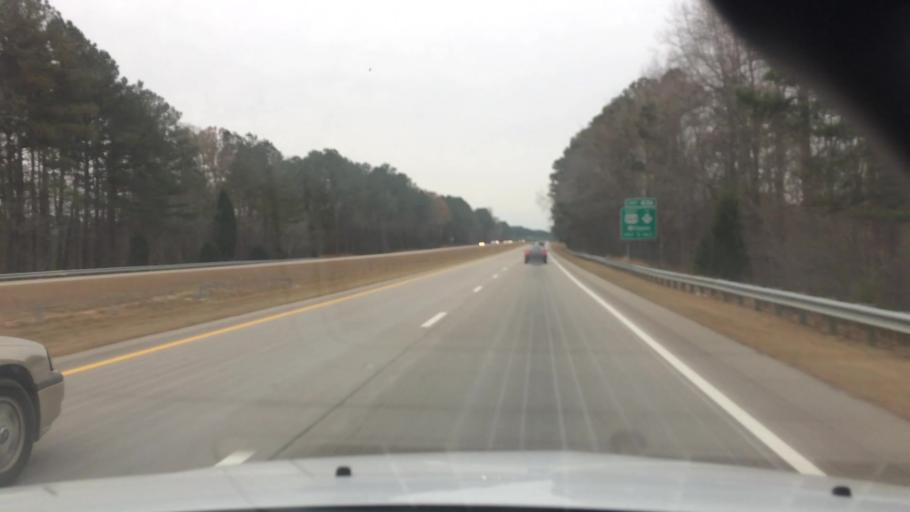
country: US
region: North Carolina
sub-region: Wake County
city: Zebulon
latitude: 35.8449
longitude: -78.2927
